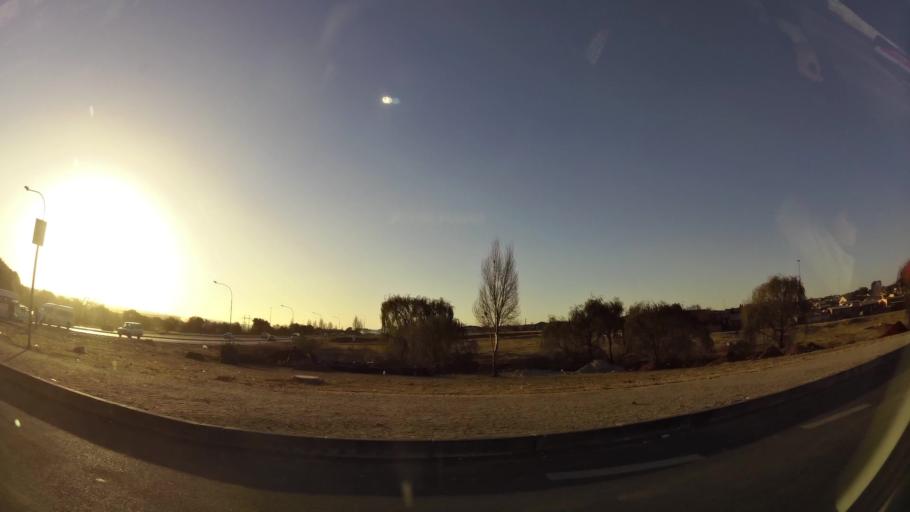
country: ZA
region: Gauteng
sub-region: Ekurhuleni Metropolitan Municipality
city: Tembisa
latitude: -26.0156
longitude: 28.2050
